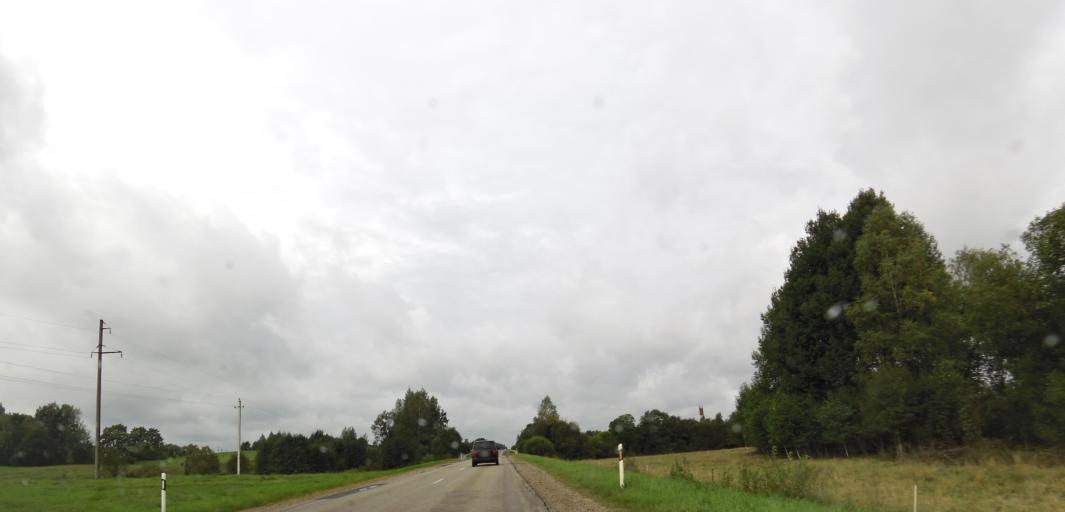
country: LT
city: Moletai
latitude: 55.2127
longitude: 25.2891
